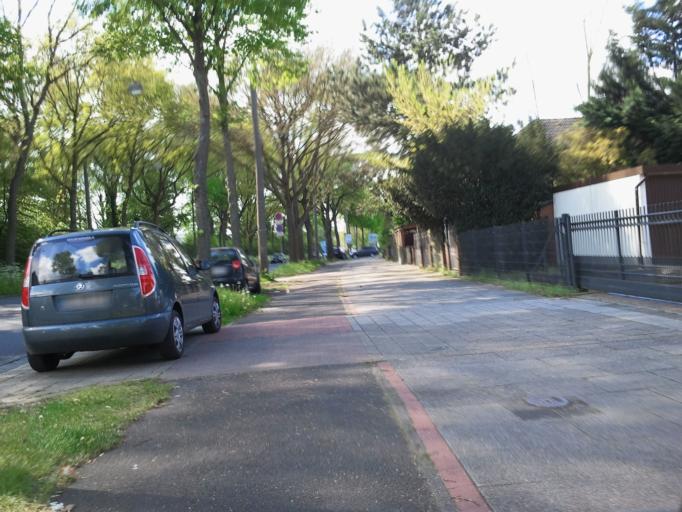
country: DE
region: Lower Saxony
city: Ritterhude
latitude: 53.1369
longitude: 8.7262
